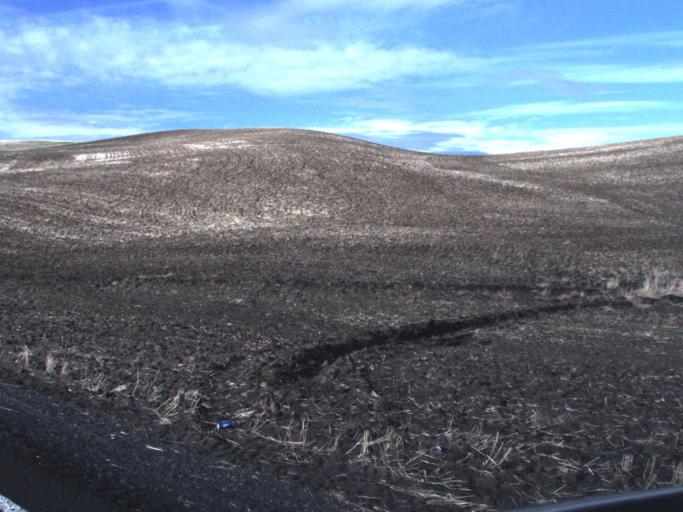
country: US
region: Washington
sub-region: Whitman County
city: Colfax
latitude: 46.9394
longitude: -117.1679
